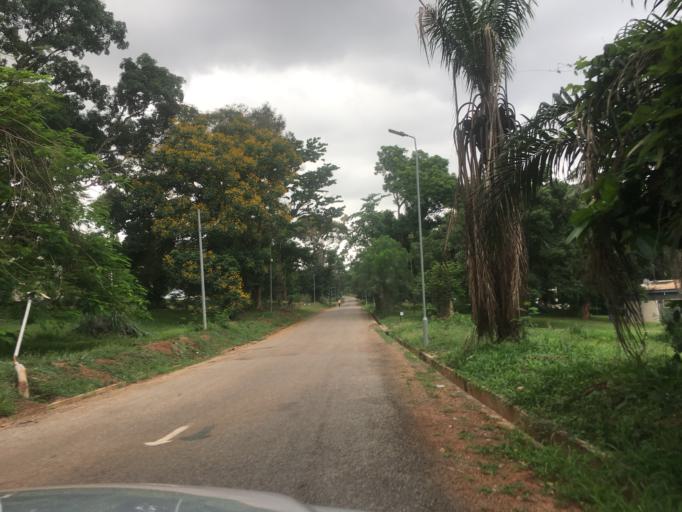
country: GH
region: Ashanti
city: Kumasi
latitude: 6.6731
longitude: -1.5849
